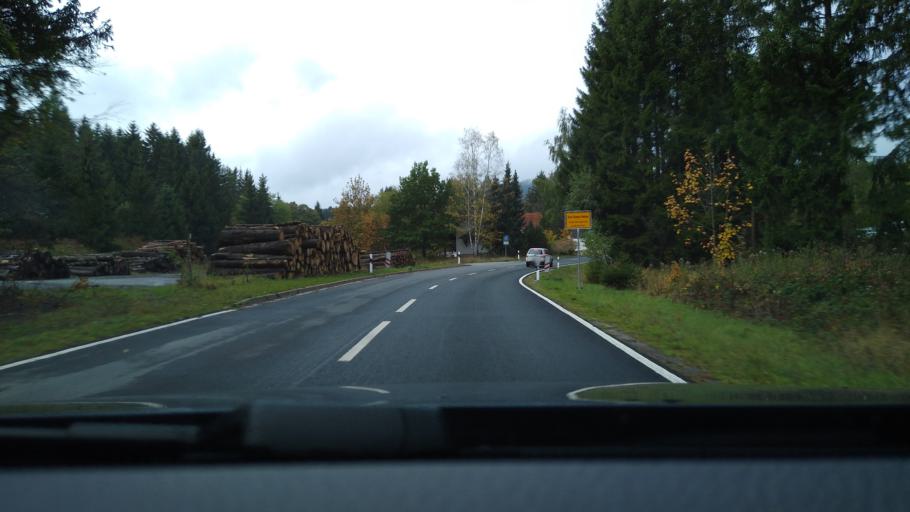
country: DE
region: Saxony-Anhalt
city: Elbingerode
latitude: 51.7708
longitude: 10.7323
